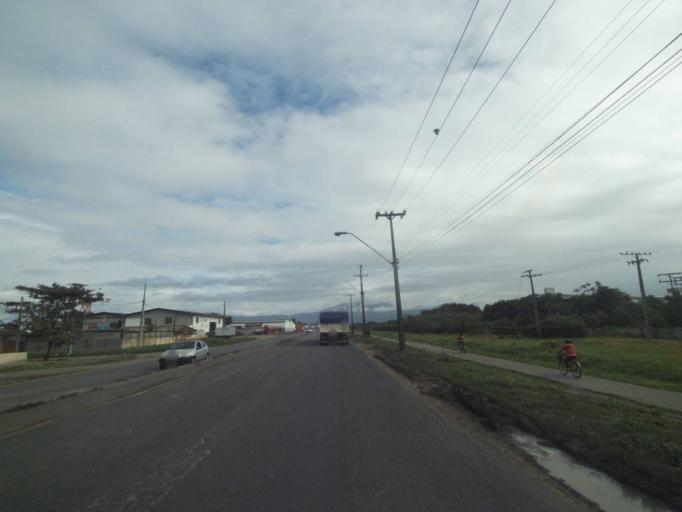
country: BR
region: Parana
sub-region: Paranagua
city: Paranagua
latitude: -25.5419
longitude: -48.5382
